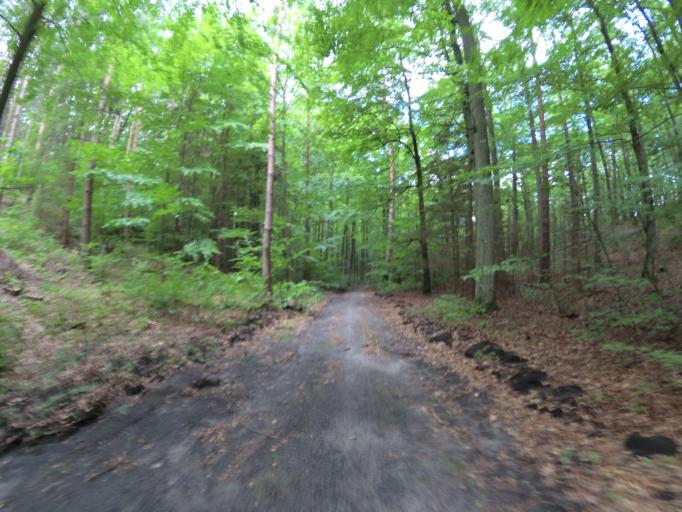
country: PL
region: Pomeranian Voivodeship
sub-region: Gdynia
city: Wielki Kack
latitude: 54.5069
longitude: 18.4442
